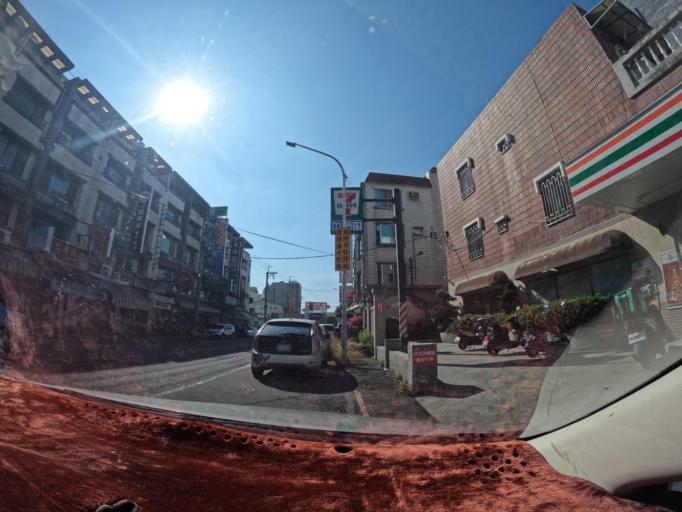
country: TW
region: Taiwan
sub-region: Tainan
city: Tainan
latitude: 23.0183
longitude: 120.2436
